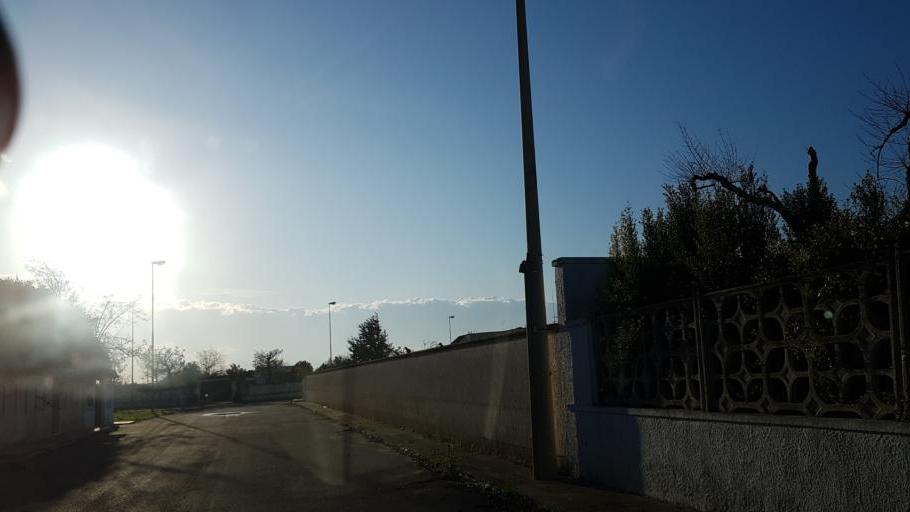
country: IT
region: Apulia
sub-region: Provincia di Brindisi
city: Torchiarolo
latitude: 40.5094
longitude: 18.0925
